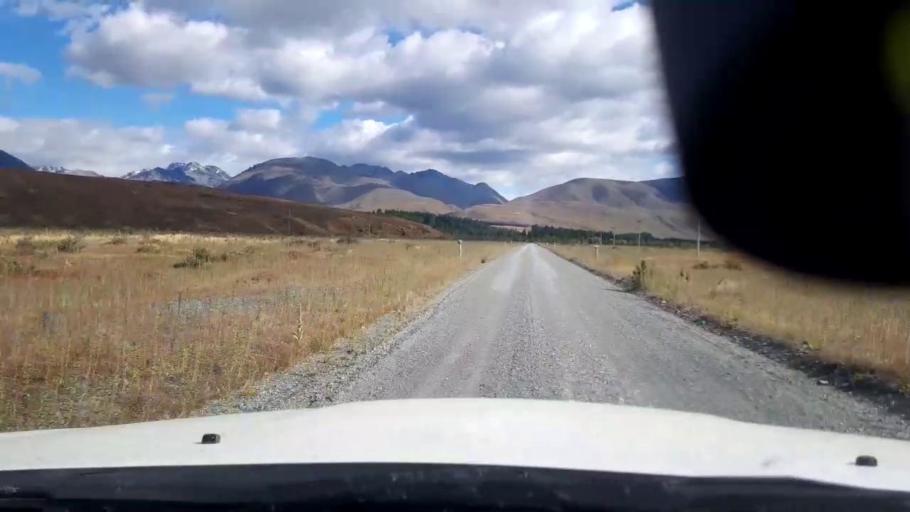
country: NZ
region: Canterbury
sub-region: Timaru District
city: Pleasant Point
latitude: -43.8861
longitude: 170.4669
